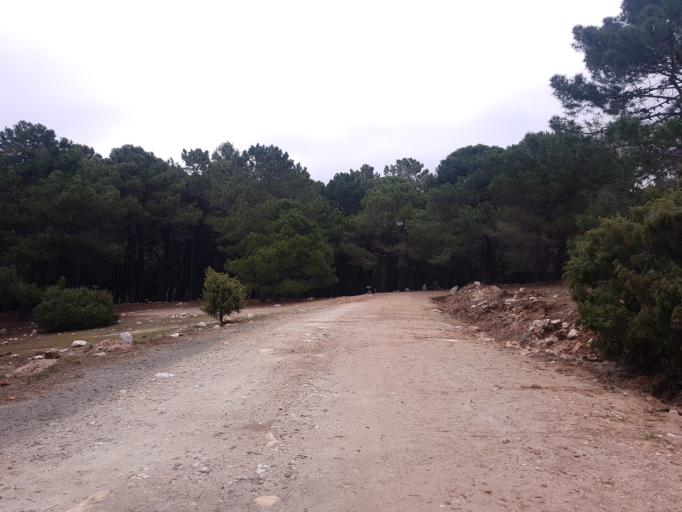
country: ES
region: Andalusia
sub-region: Provincia de Malaga
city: Ojen
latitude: 36.5671
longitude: -4.8912
